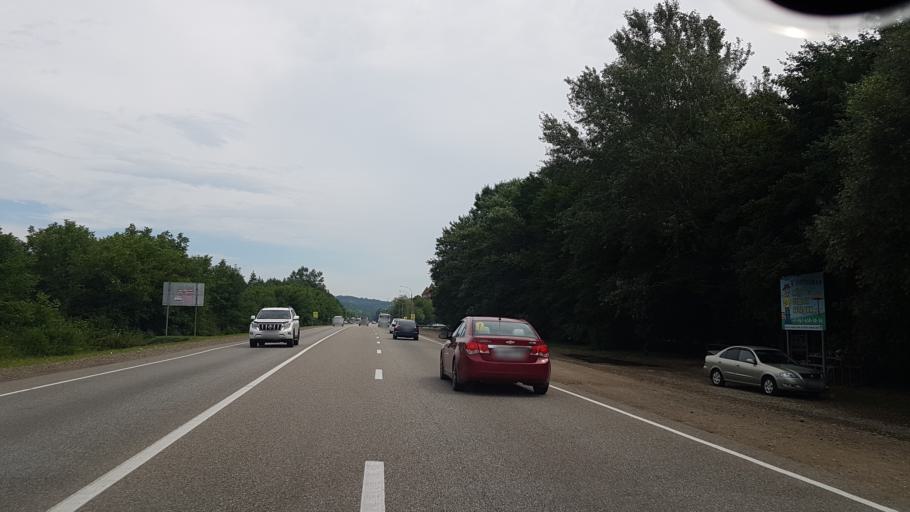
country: RU
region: Krasnodarskiy
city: Goryachiy Klyuch
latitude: 44.6192
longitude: 39.0879
